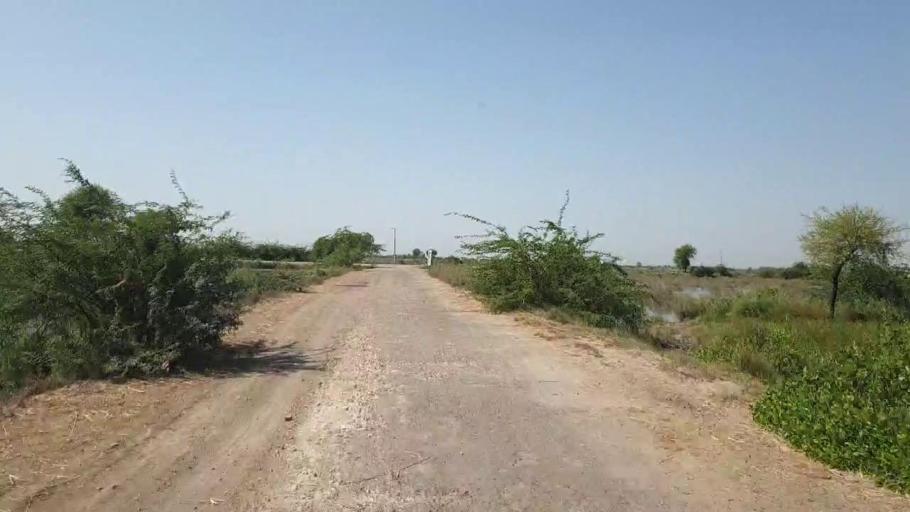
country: PK
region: Sindh
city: Tando Bago
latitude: 24.7322
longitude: 68.9981
